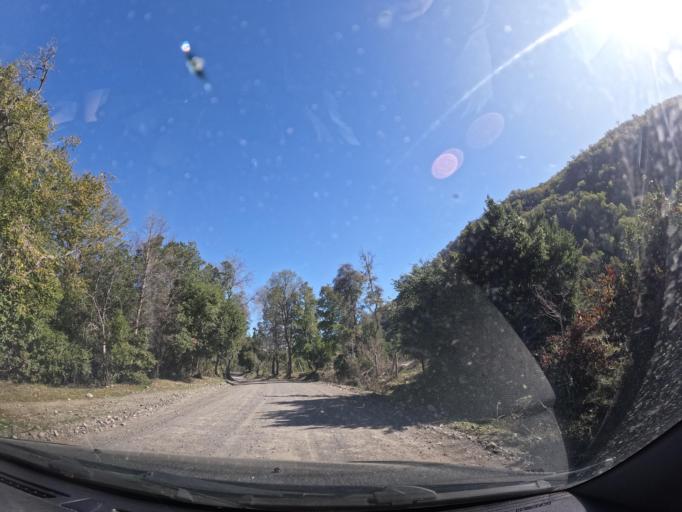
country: CL
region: Maule
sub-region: Provincia de Linares
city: Longavi
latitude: -36.2288
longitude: -71.3979
